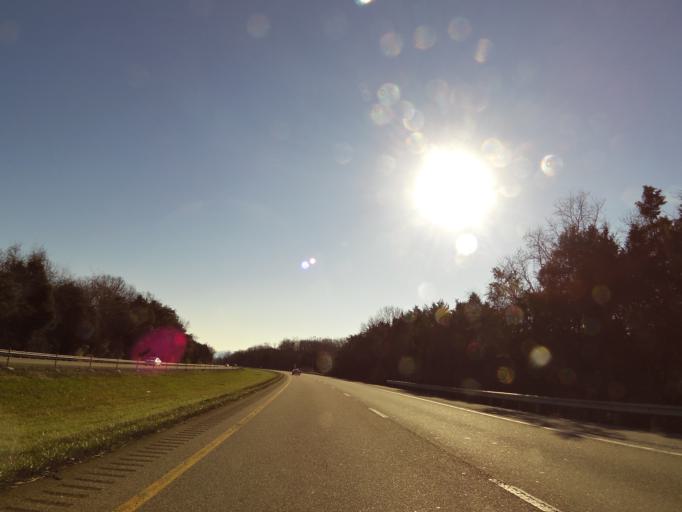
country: US
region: Tennessee
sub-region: Jefferson County
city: Dandridge
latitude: 36.0596
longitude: -83.3749
